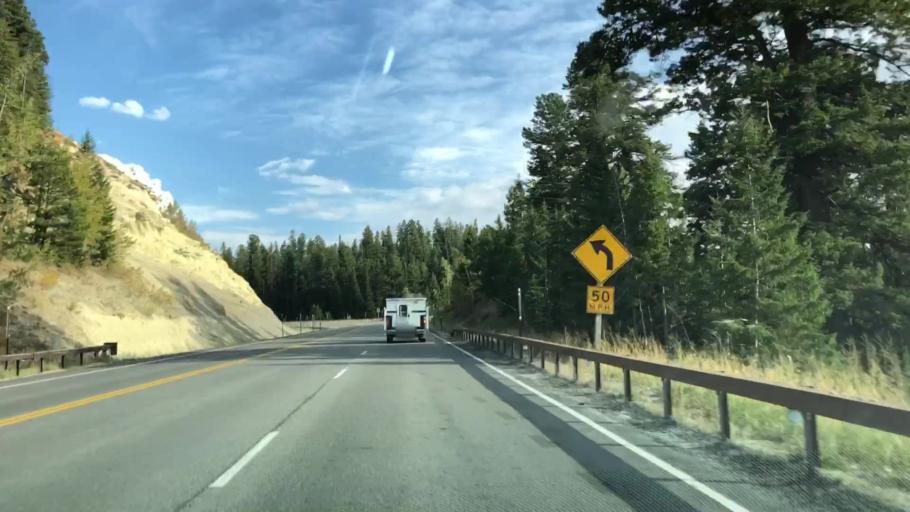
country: US
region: Wyoming
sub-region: Sublette County
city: Pinedale
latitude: 43.1344
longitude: -110.2065
